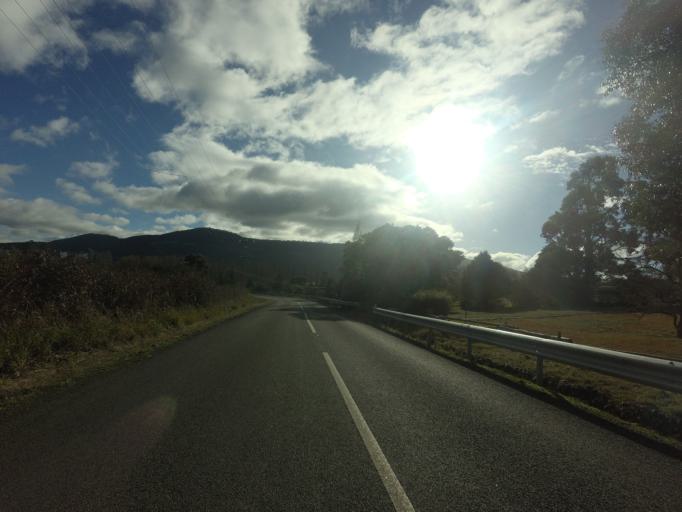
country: AU
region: Tasmania
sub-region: Derwent Valley
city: New Norfolk
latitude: -42.7844
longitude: 147.1171
